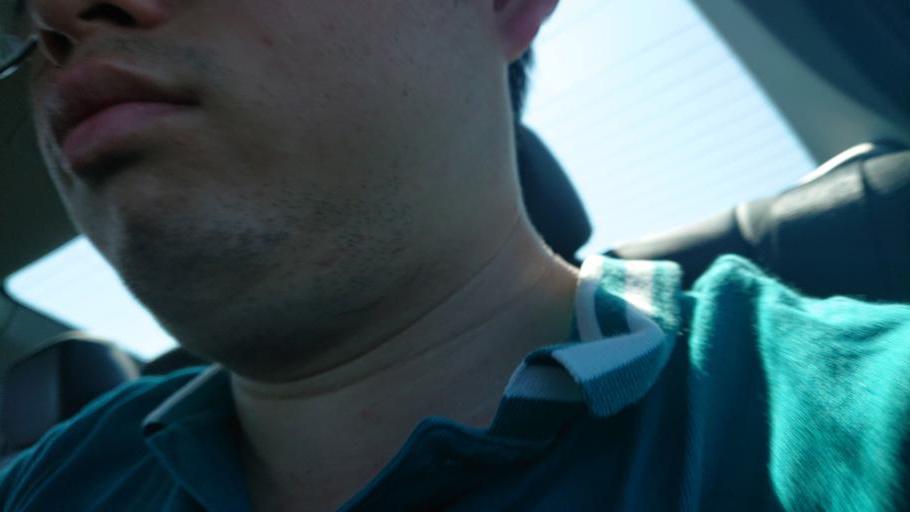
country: TW
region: Taiwan
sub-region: Chiayi
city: Taibao
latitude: 23.7115
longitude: 120.1884
